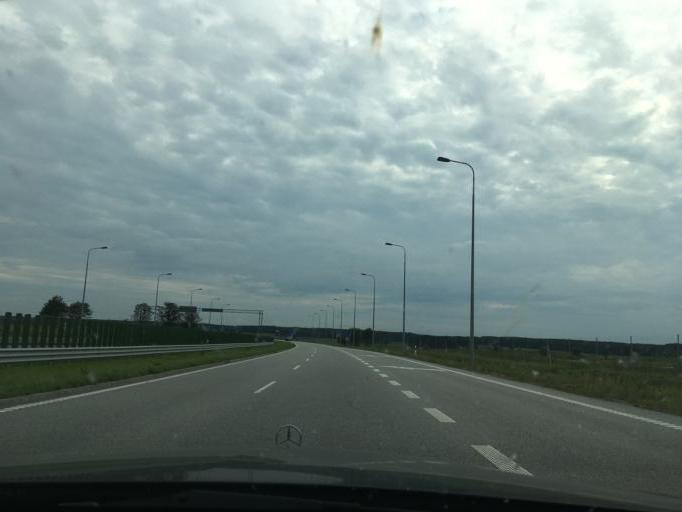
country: PL
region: Podlasie
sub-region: Powiat kolnenski
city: Stawiski
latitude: 53.3853
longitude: 22.1435
